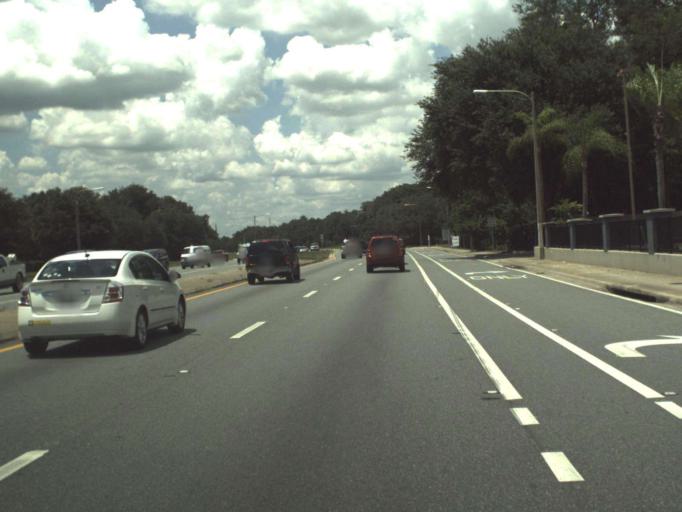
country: US
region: Florida
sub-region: Orange County
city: Orlando
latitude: 28.5540
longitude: -81.4137
